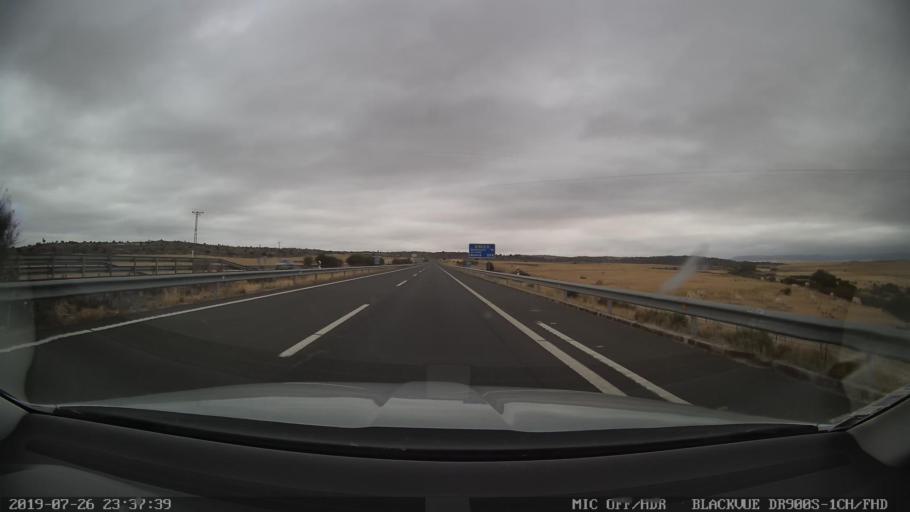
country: ES
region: Extremadura
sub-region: Provincia de Caceres
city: Trujillo
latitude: 39.4164
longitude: -5.8856
